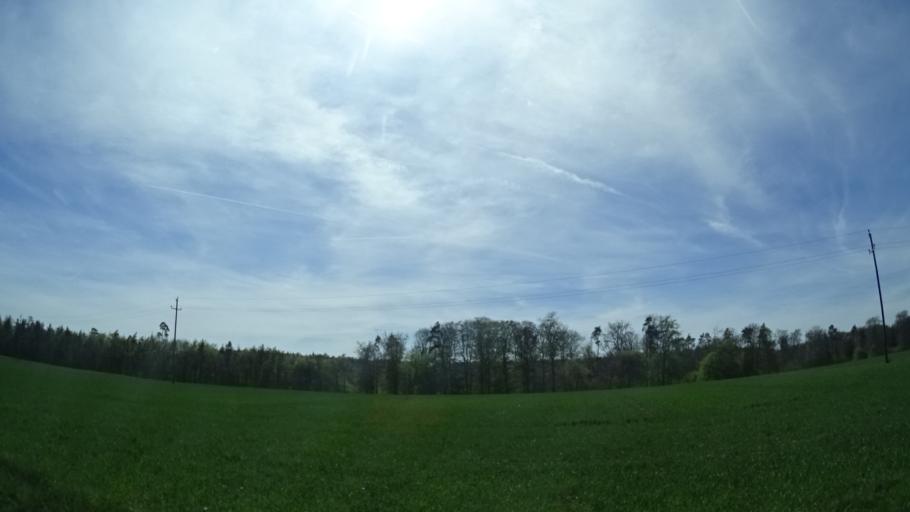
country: DE
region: Bavaria
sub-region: Regierungsbezirk Unterfranken
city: Maroldsweisach
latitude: 50.1769
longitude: 10.6274
